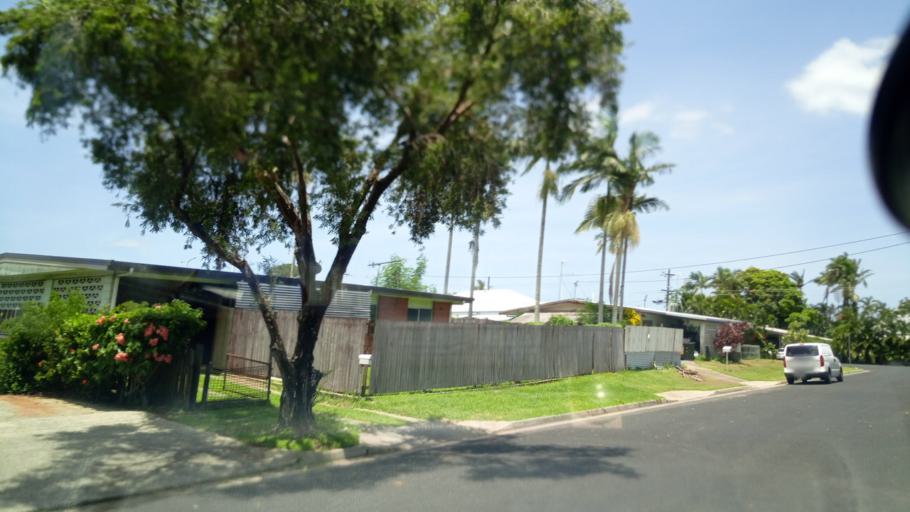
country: AU
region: Queensland
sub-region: Cairns
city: Woree
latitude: -16.9399
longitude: 145.7456
